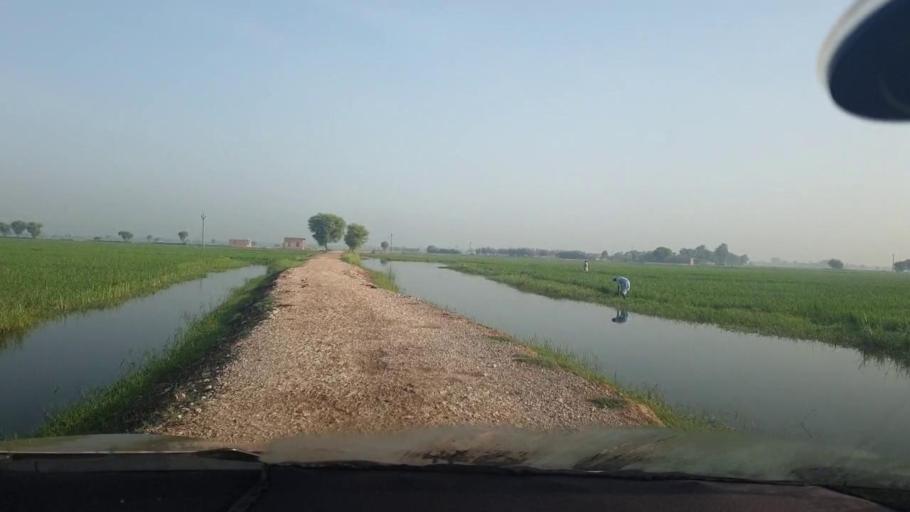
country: PK
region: Sindh
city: Kambar
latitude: 27.6306
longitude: 68.0172
